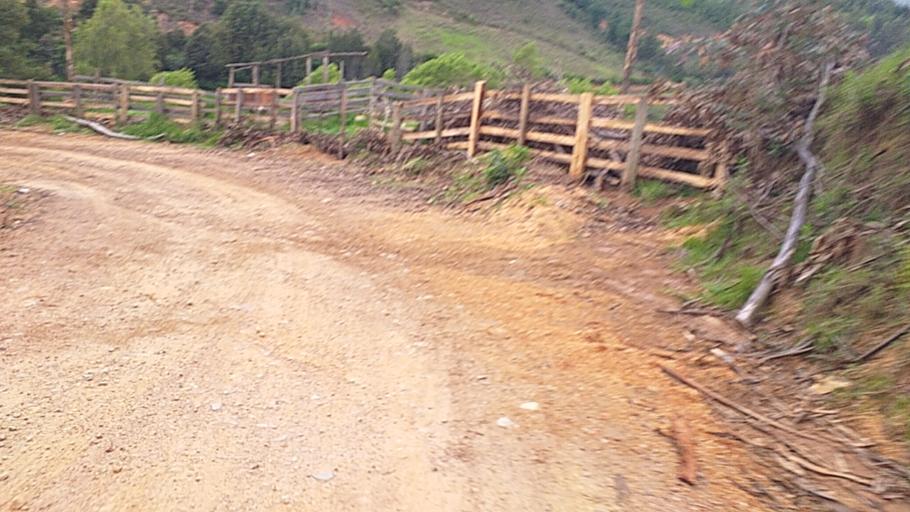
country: CO
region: Boyaca
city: Floresta
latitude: 5.8759
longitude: -72.9154
